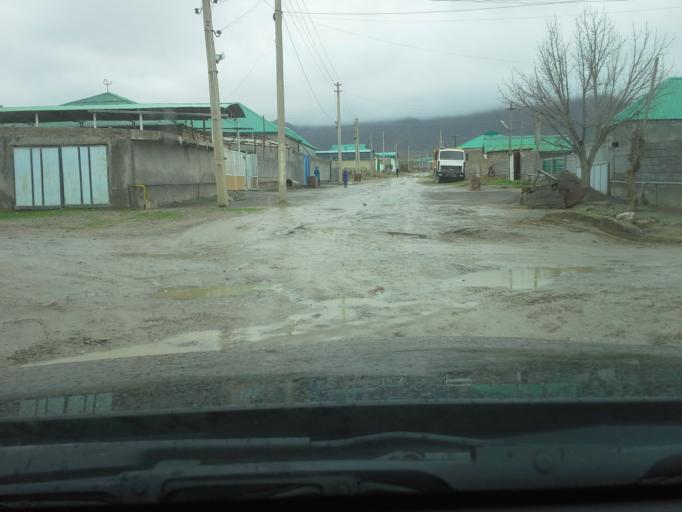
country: TM
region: Ahal
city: Abadan
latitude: 37.9685
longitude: 58.2073
